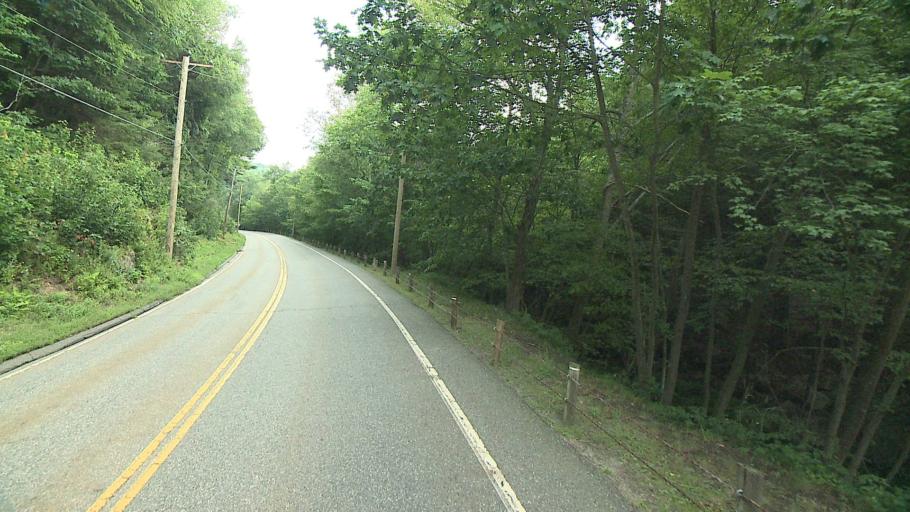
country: US
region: Connecticut
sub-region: Litchfield County
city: Bethlehem Village
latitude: 41.6729
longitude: -73.1479
